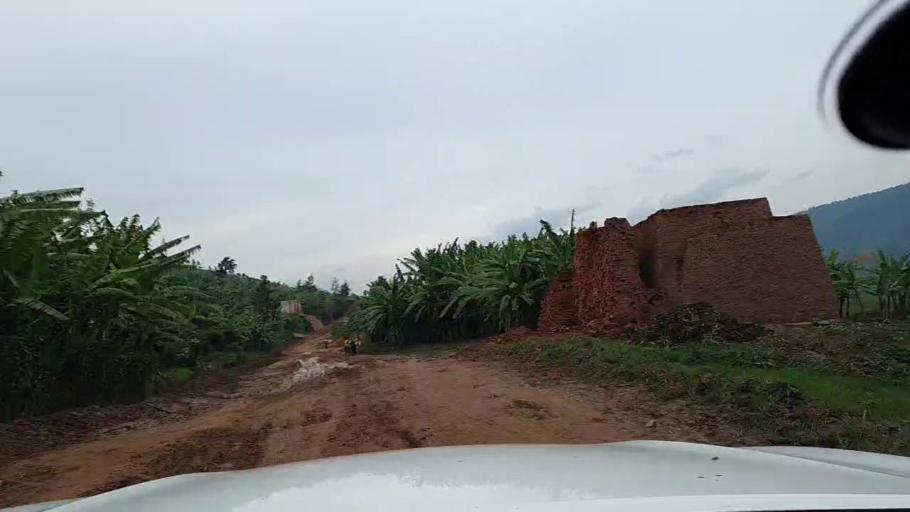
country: RW
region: Kigali
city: Kigali
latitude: -1.9480
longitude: 29.9896
